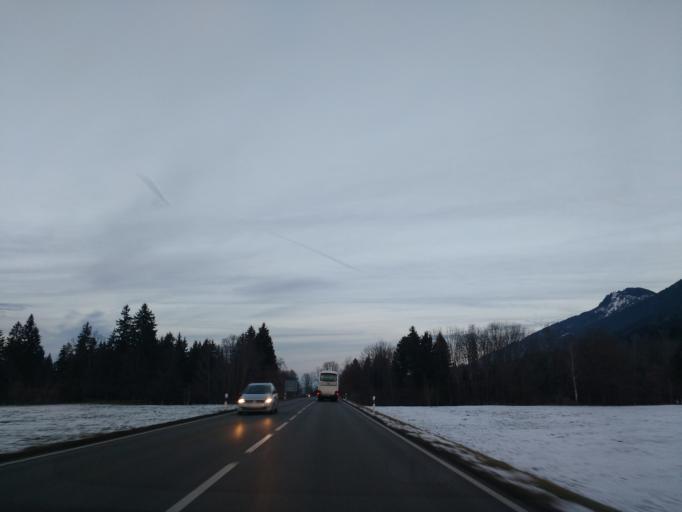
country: DE
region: Bavaria
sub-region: Swabia
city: Halblech
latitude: 47.6252
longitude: 10.8167
